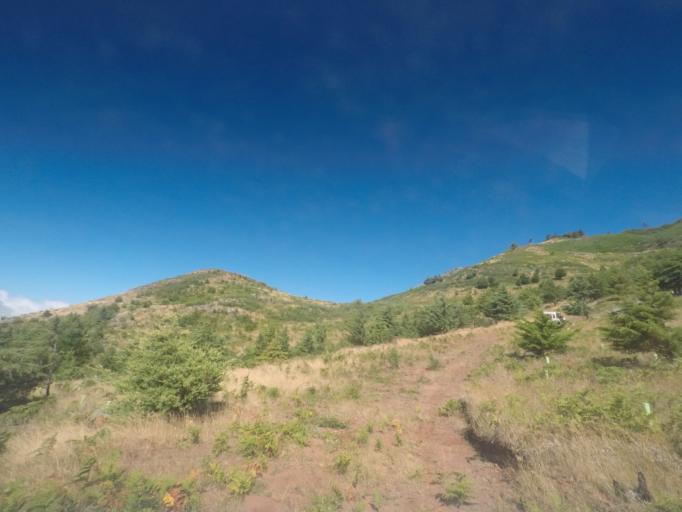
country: PT
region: Madeira
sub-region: Funchal
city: Nossa Senhora do Monte
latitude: 32.7024
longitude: -16.9107
